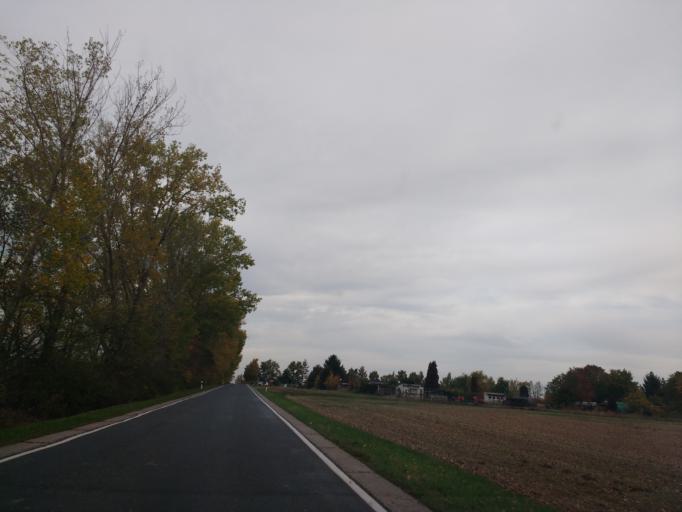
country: DE
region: Thuringia
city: Seebach
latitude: 51.1753
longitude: 10.5088
